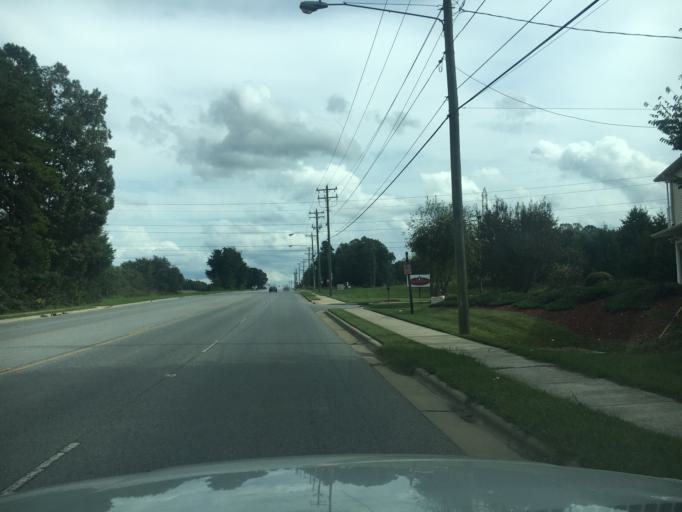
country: US
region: North Carolina
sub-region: Gaston County
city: Bessemer City
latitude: 35.2814
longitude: -81.2378
